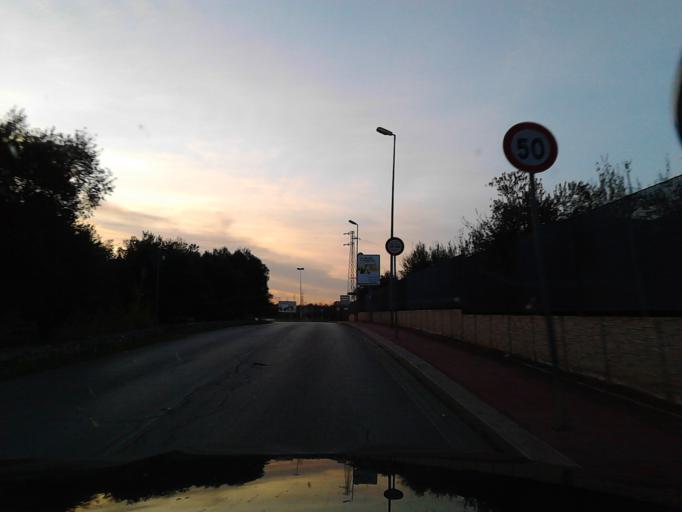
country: IT
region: Apulia
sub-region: Provincia di Bari
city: Lamie
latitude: 41.0405
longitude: 16.8747
